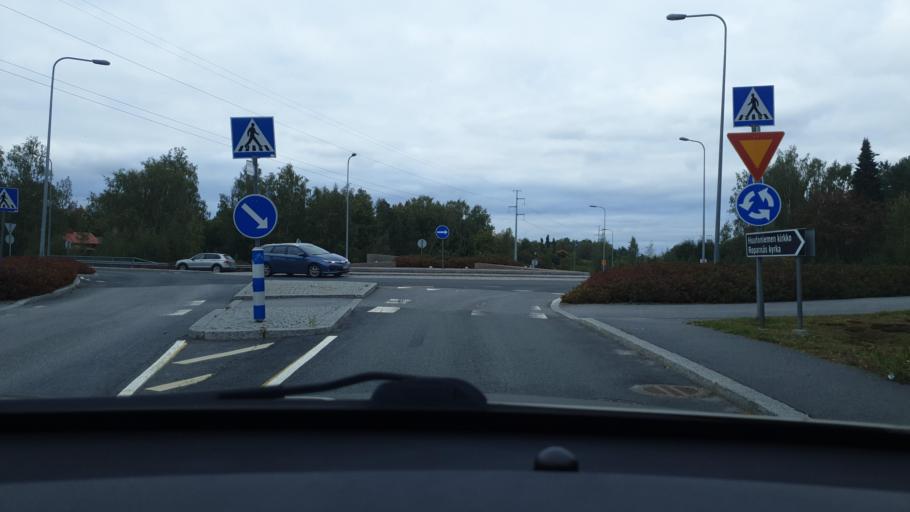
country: FI
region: Ostrobothnia
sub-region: Vaasa
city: Korsholm
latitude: 63.0986
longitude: 21.6612
